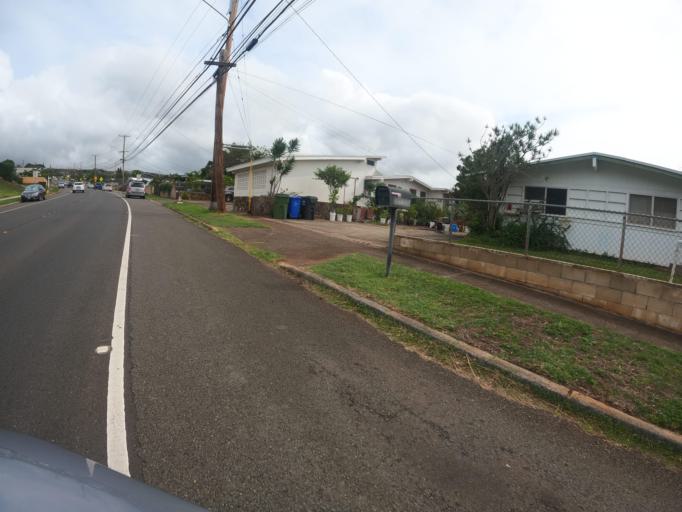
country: US
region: Hawaii
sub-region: Honolulu County
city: Halawa Heights
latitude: 21.3756
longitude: -157.9178
